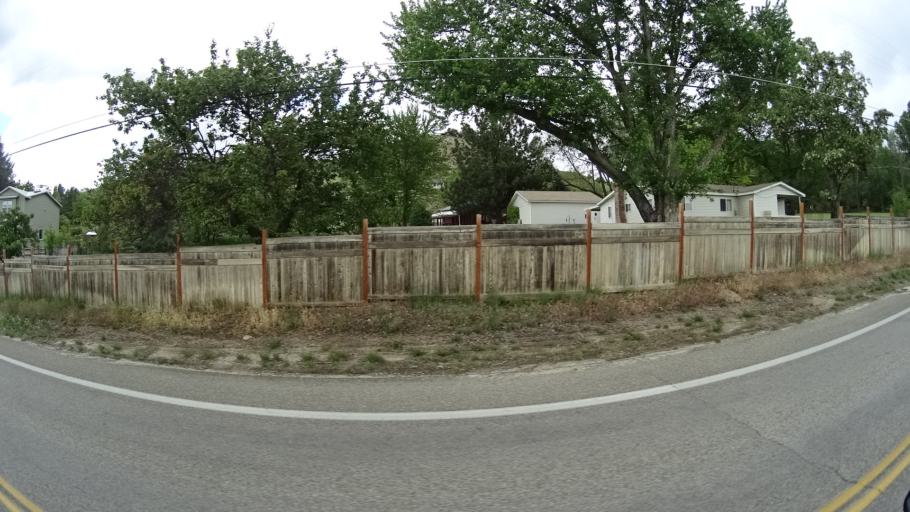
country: US
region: Idaho
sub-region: Ada County
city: Garden City
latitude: 43.6750
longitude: -116.2617
